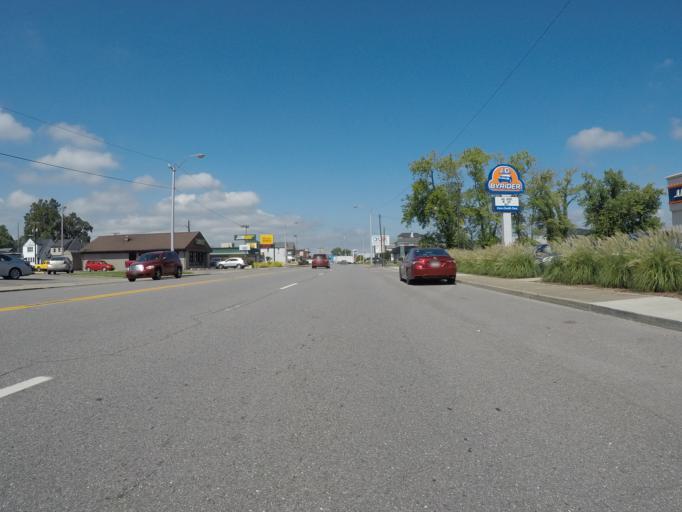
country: US
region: Kentucky
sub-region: Boyd County
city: Ashland
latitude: 38.4705
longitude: -82.6240
